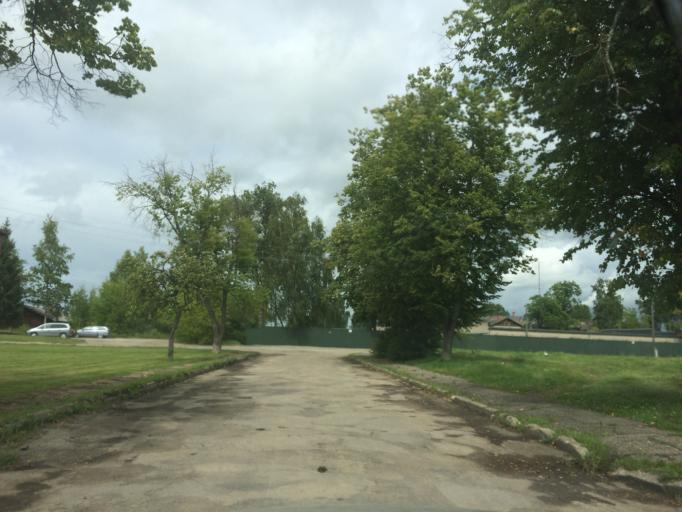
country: LV
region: Rezekne
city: Rezekne
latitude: 56.5017
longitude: 27.3166
